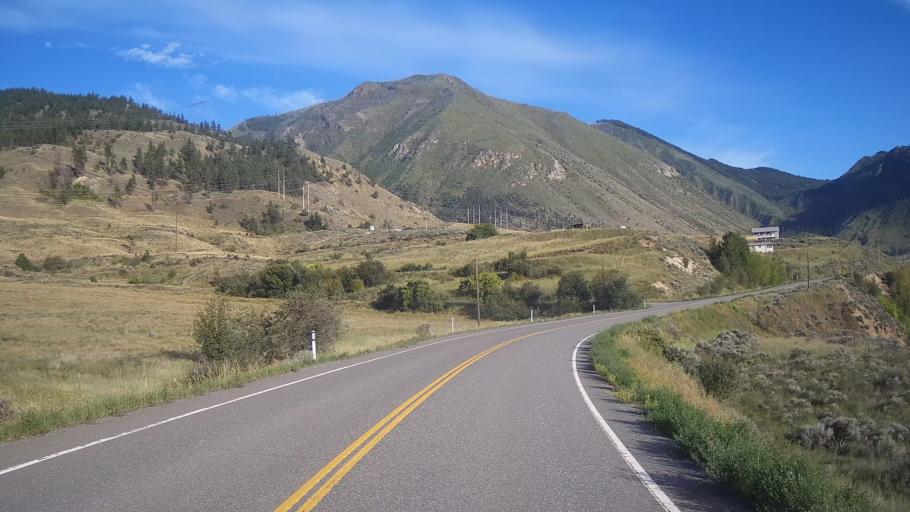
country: CA
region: British Columbia
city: Lillooet
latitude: 50.7669
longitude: -121.8365
